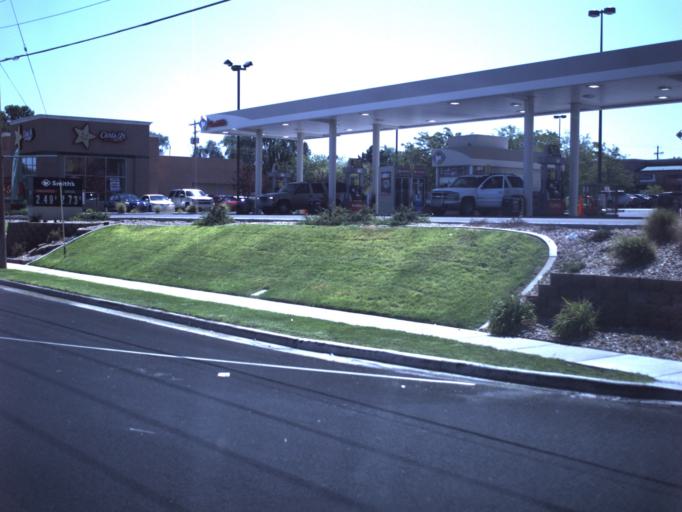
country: US
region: Utah
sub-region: Salt Lake County
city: Magna
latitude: 40.6964
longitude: -112.0836
